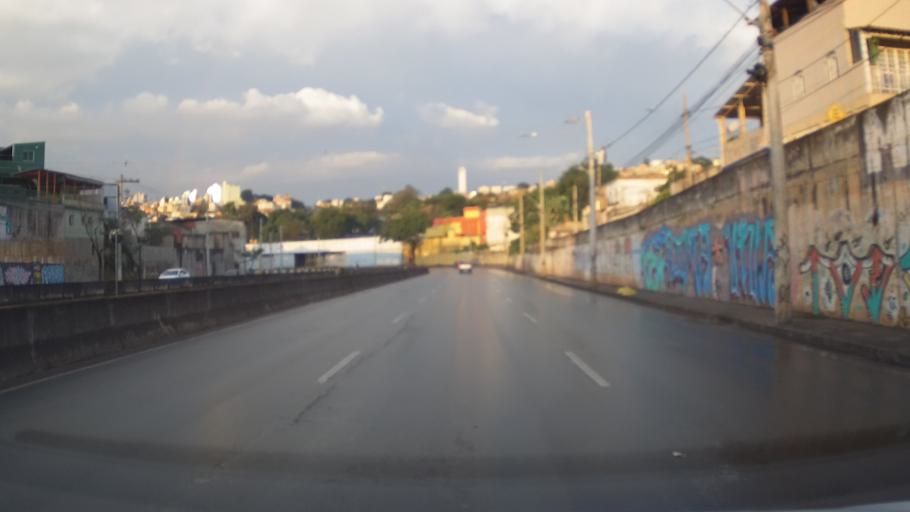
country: BR
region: Minas Gerais
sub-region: Belo Horizonte
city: Belo Horizonte
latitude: -19.9527
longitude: -43.9844
